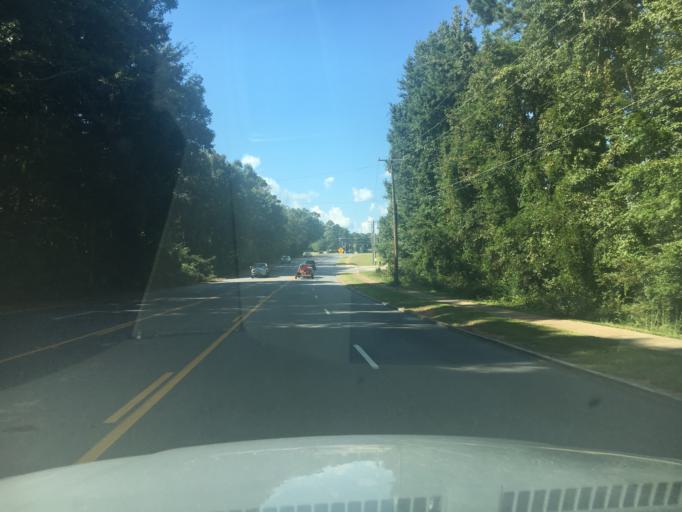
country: US
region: South Carolina
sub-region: Greenwood County
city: Greenwood
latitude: 34.2286
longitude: -82.1762
